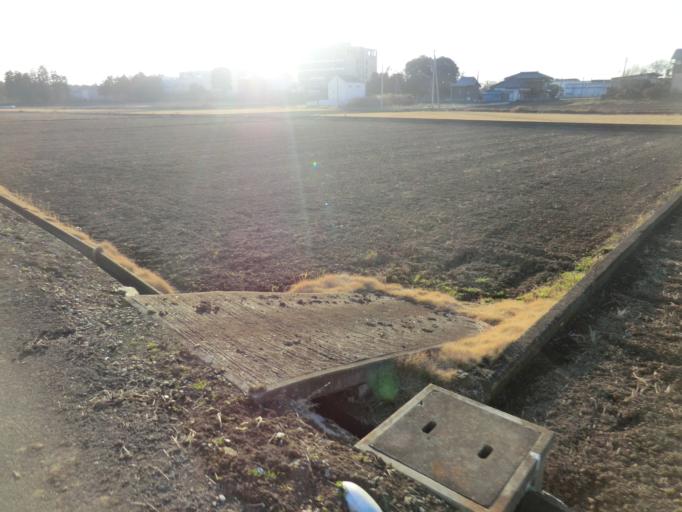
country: JP
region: Ibaraki
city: Naka
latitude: 36.0873
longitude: 140.0717
